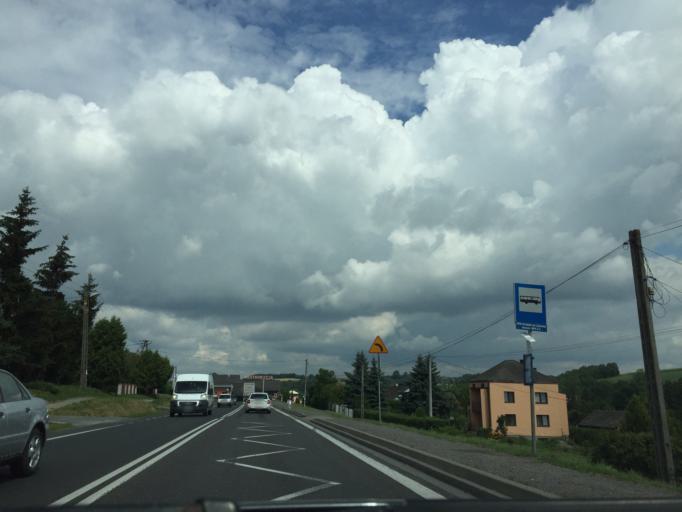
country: PL
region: Lesser Poland Voivodeship
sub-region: Powiat krakowski
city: Michalowice
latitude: 50.1514
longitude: 19.9838
